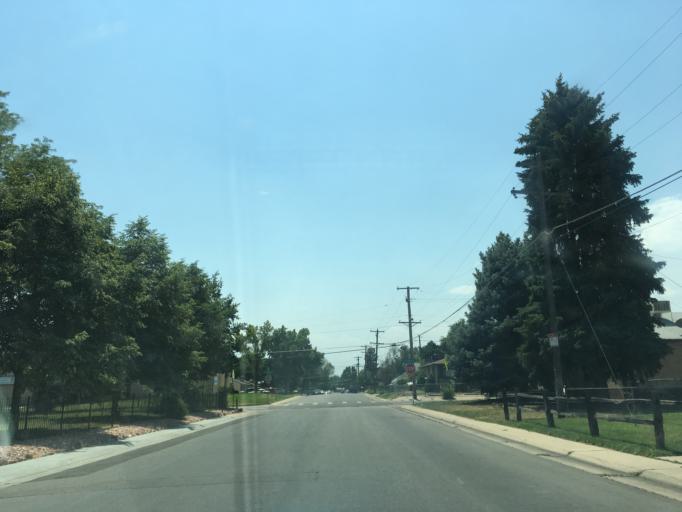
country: US
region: Colorado
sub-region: Arapahoe County
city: Sheridan
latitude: 39.6937
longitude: -105.0320
